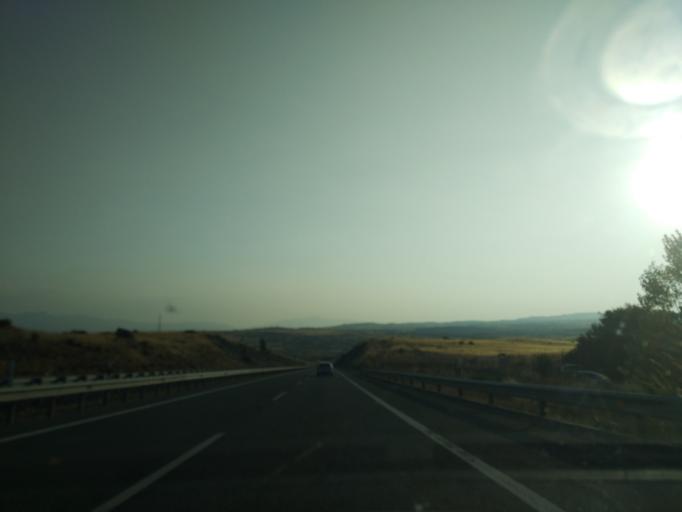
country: ES
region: Castille and Leon
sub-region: Provincia de Avila
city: Avila
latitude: 40.6761
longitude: -4.6964
